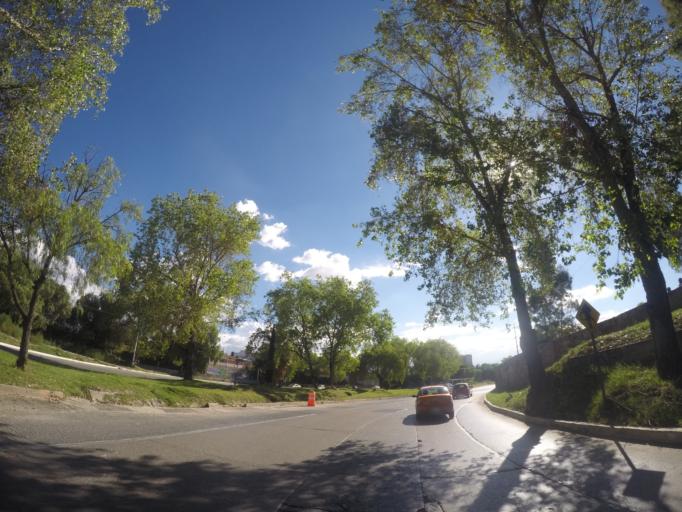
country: MX
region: San Luis Potosi
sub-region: San Luis Potosi
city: San Luis Potosi
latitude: 22.1641
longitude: -100.9879
